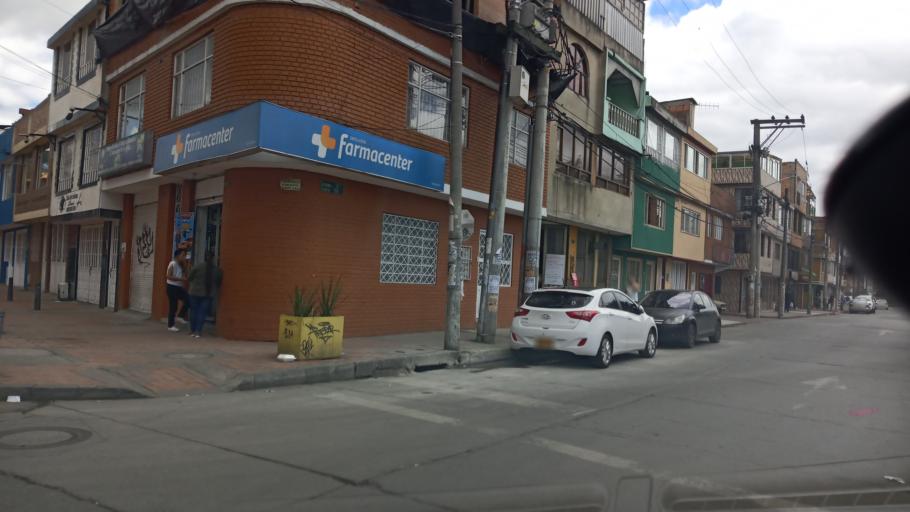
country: CO
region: Cundinamarca
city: Funza
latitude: 4.6696
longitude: -74.1500
